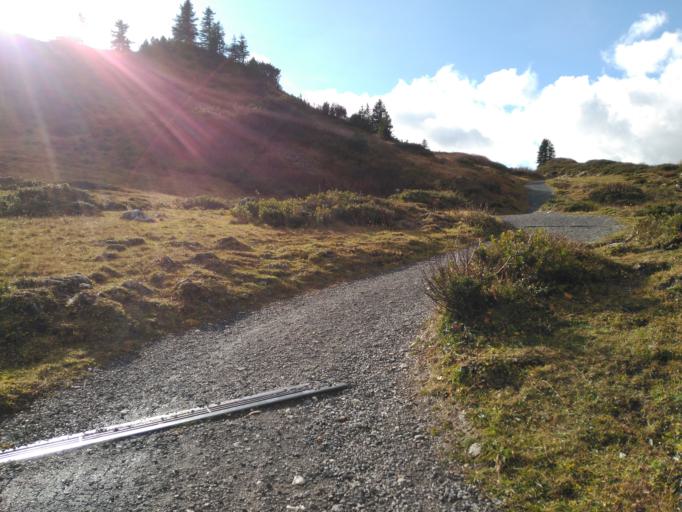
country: AT
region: Vorarlberg
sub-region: Politischer Bezirk Bregenz
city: Schroecken
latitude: 47.2635
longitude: 10.1154
